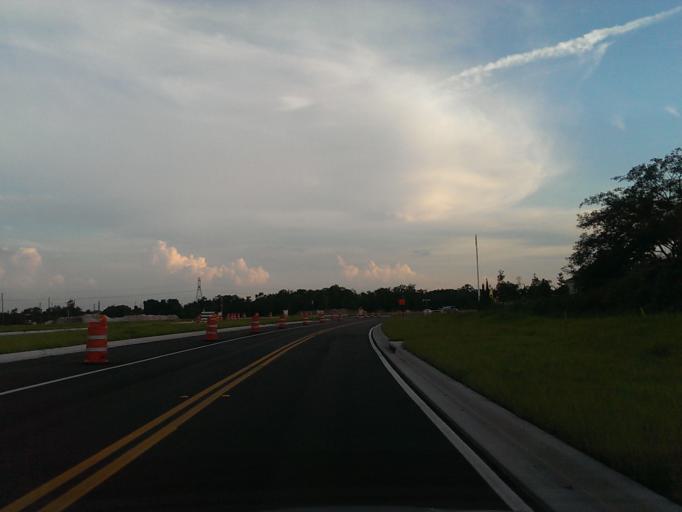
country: US
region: Florida
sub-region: Orange County
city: Lake Butler
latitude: 28.4706
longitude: -81.5834
